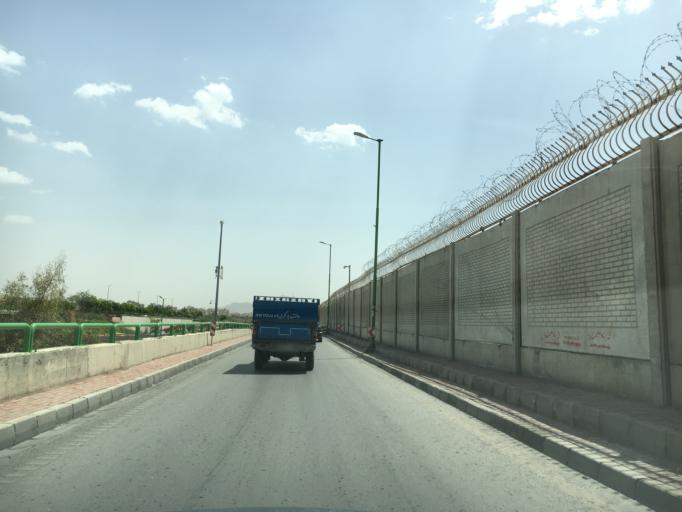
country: IR
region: Isfahan
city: Isfahan
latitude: 32.6227
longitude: 51.6977
